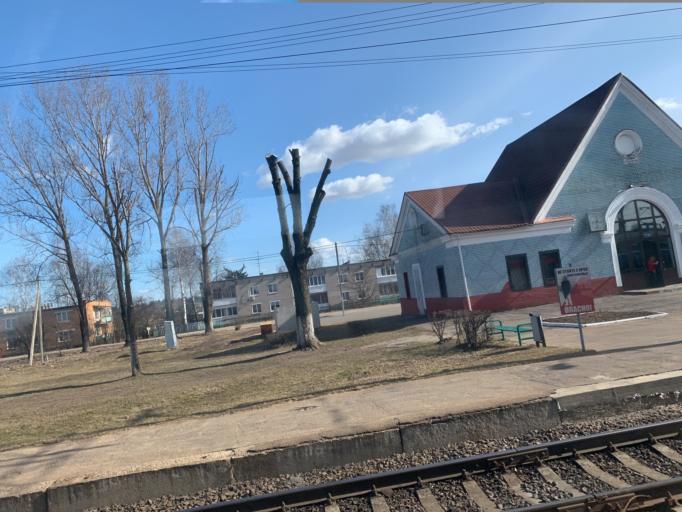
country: BY
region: Minsk
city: Shchomyslitsa
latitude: 53.8155
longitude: 27.4536
